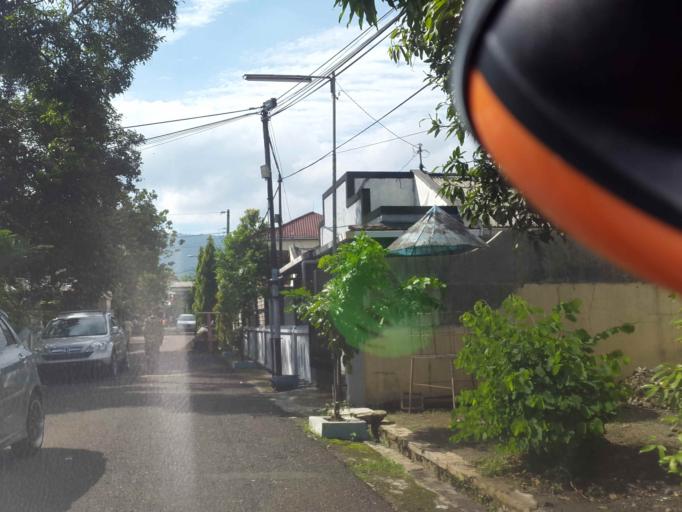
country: ID
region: Central Java
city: Wonosobo
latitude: -7.3896
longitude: 109.7240
